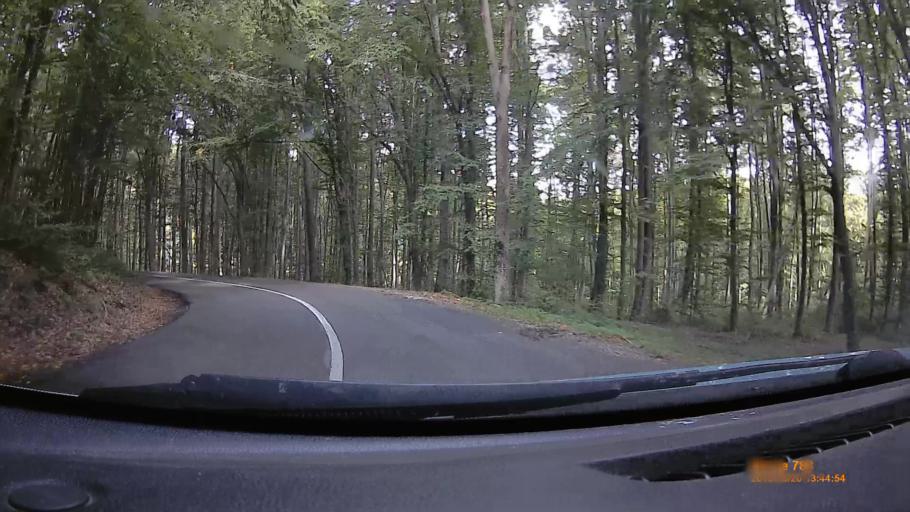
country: HU
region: Borsod-Abauj-Zemplen
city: Saly
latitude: 48.0617
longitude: 20.5637
